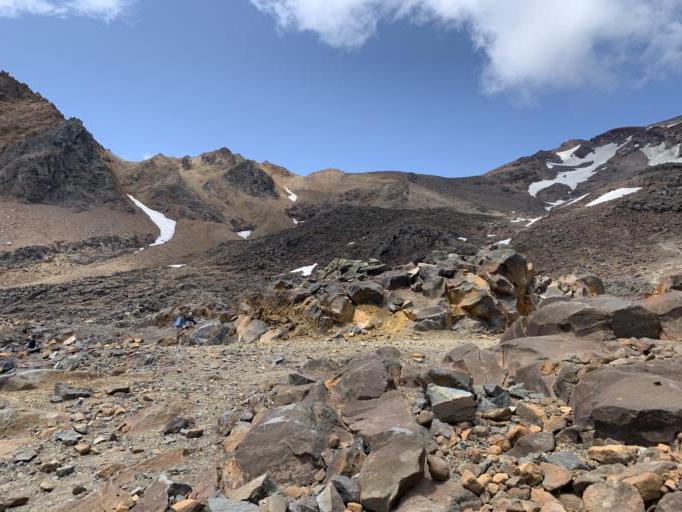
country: NZ
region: Manawatu-Wanganui
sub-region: Ruapehu District
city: Waiouru
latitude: -39.2528
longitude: 175.5638
